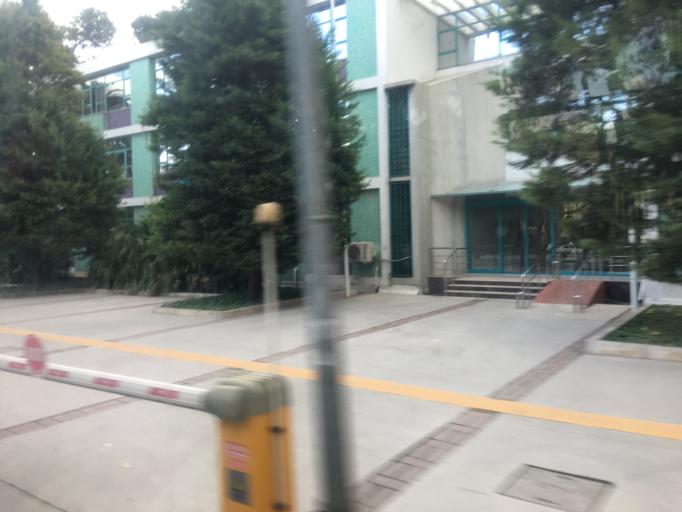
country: TR
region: Izmir
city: Izmir
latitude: 38.4289
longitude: 27.1416
